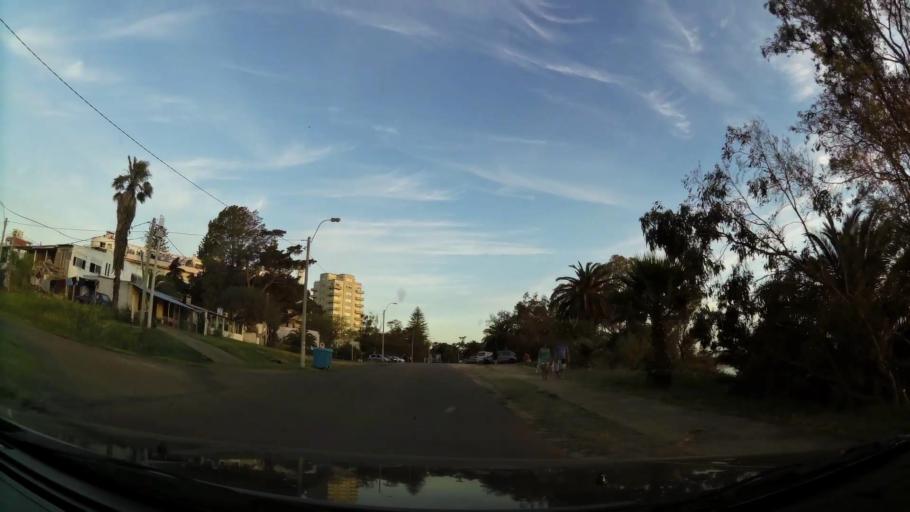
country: UY
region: Canelones
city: Atlantida
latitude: -34.7744
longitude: -55.7651
